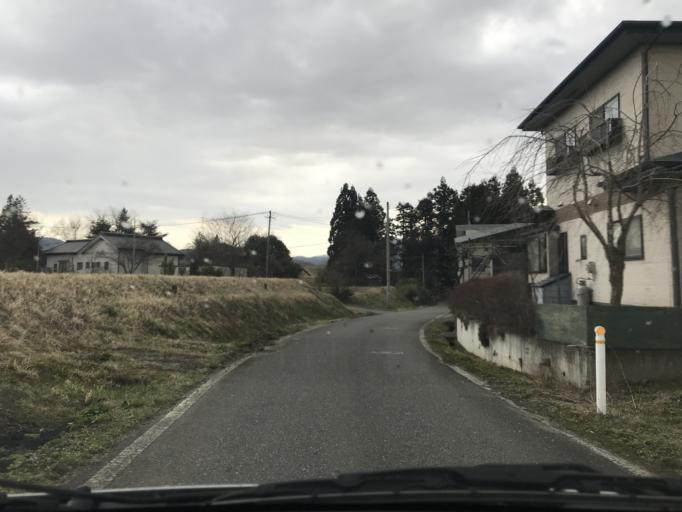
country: JP
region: Iwate
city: Mizusawa
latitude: 39.0785
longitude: 141.1678
